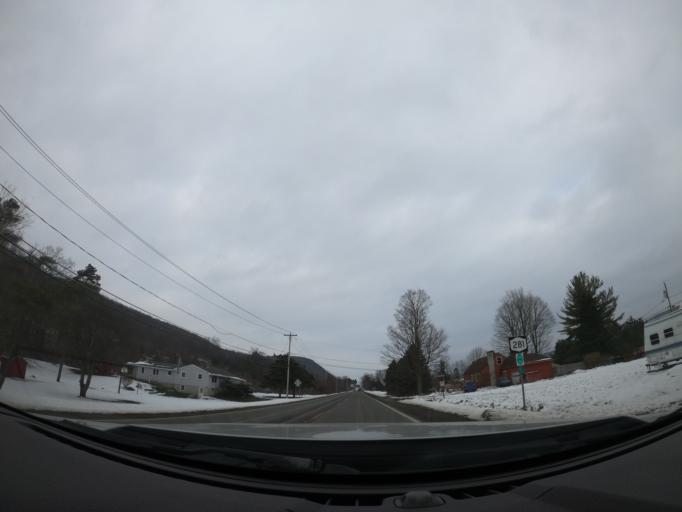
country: US
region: New York
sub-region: Cortland County
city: Homer
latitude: 42.6978
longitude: -76.1636
